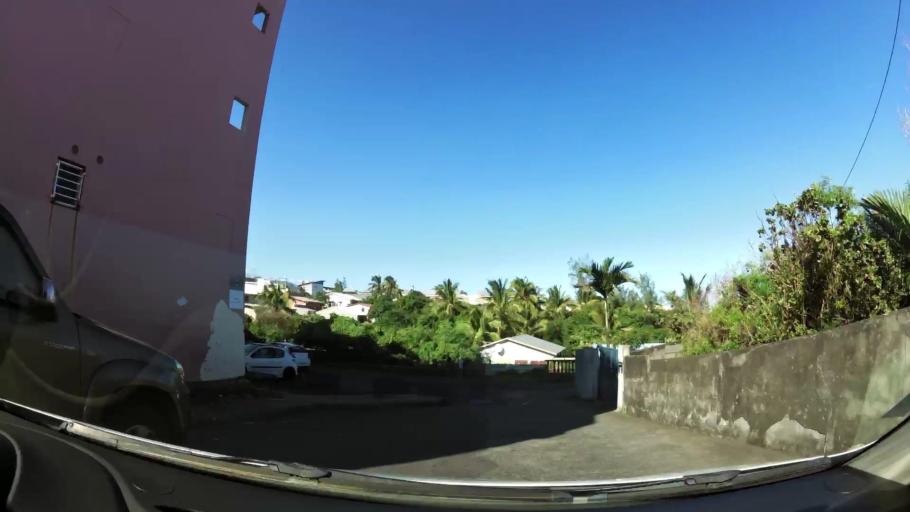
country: RE
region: Reunion
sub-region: Reunion
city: Saint-Pierre
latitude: -21.3472
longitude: 55.4874
